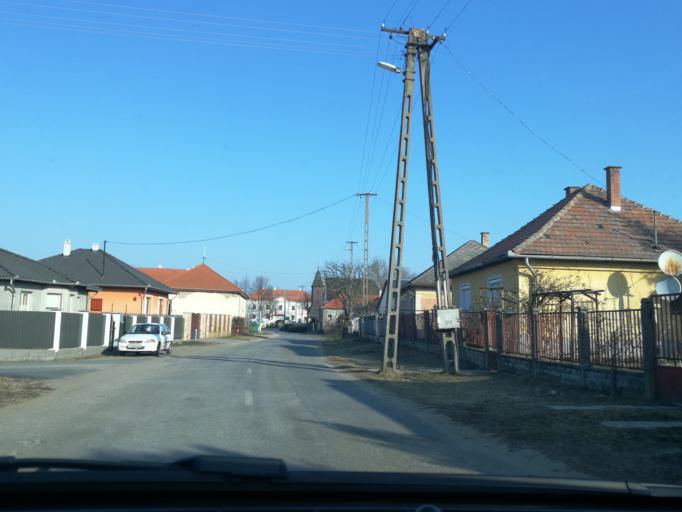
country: HU
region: Szabolcs-Szatmar-Bereg
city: Nyirbogdany
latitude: 48.0570
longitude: 21.9353
